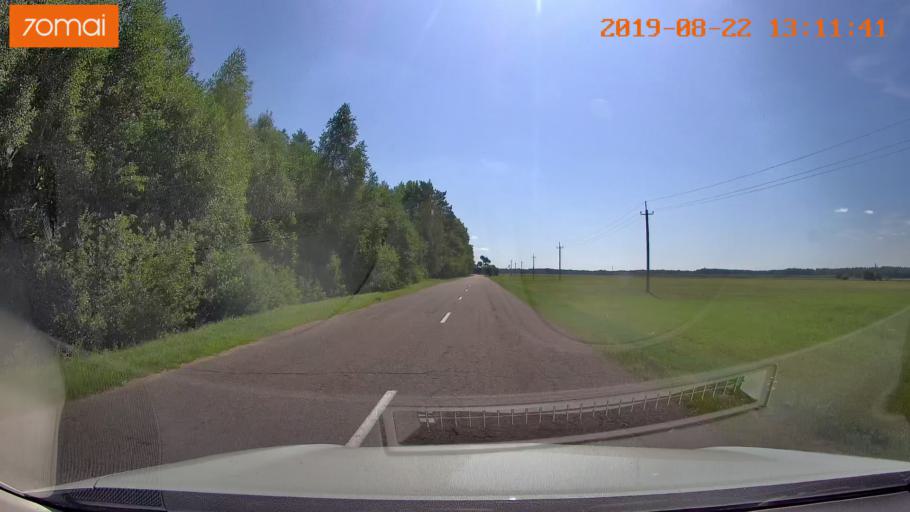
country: BY
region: Minsk
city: Prawdzinski
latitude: 53.2769
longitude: 27.8541
